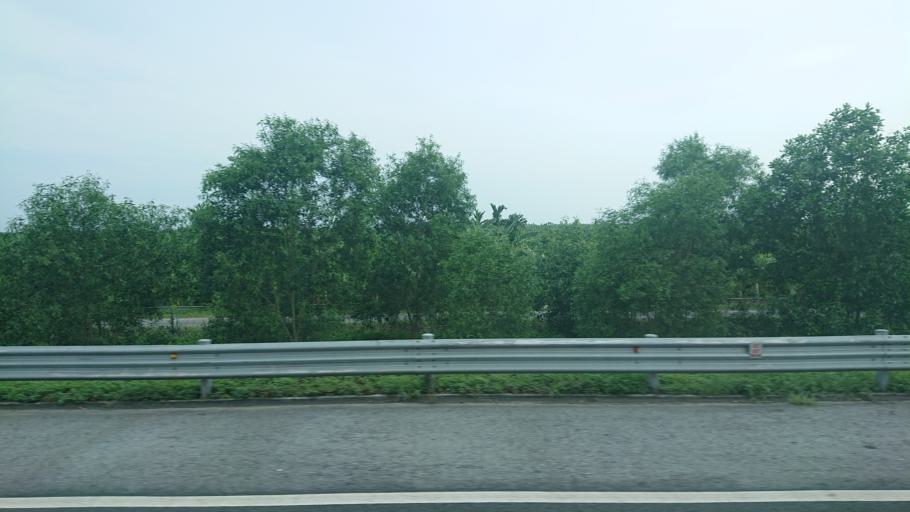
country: VN
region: Hai Duong
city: Tu Ky
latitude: 20.8260
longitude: 106.4619
